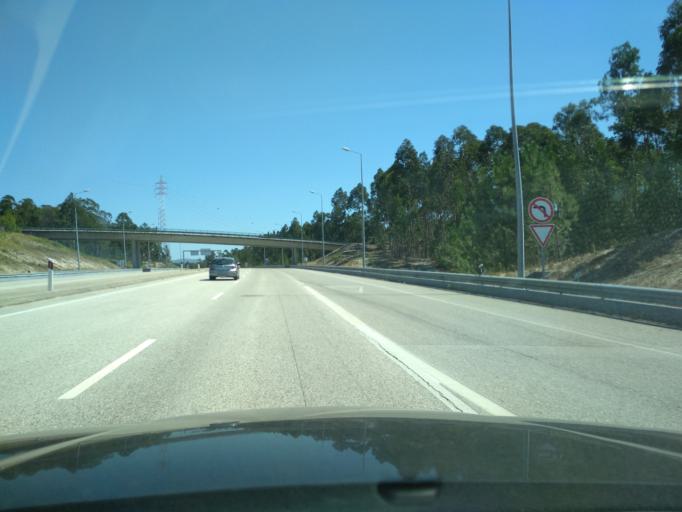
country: PT
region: Leiria
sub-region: Pombal
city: Lourical
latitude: 39.9834
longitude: -8.7284
